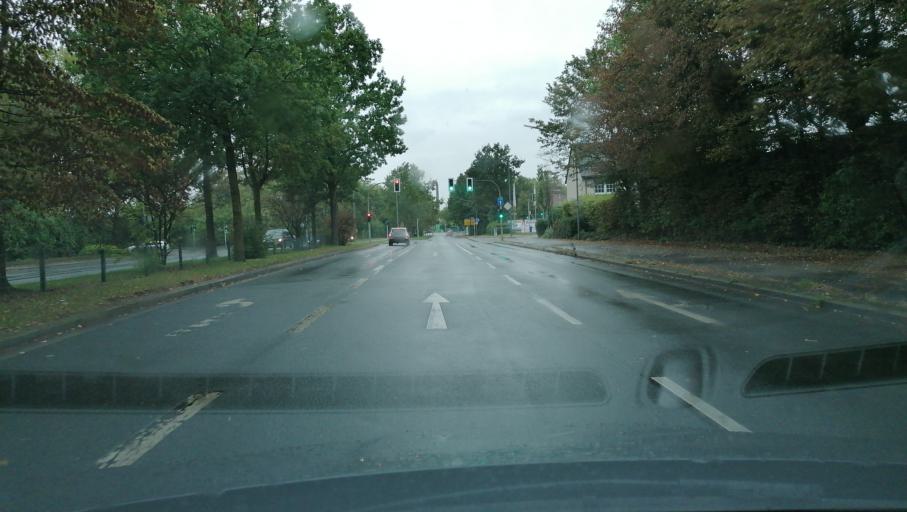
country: DE
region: North Rhine-Westphalia
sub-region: Regierungsbezirk Munster
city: Gelsenkirchen
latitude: 51.5213
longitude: 7.0652
